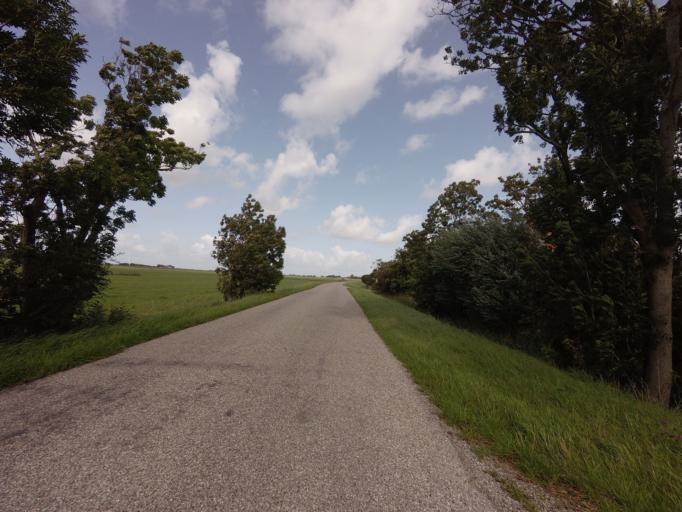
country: NL
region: Friesland
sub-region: Gemeente Franekeradeel
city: Sexbierum
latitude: 53.1607
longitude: 5.4836
